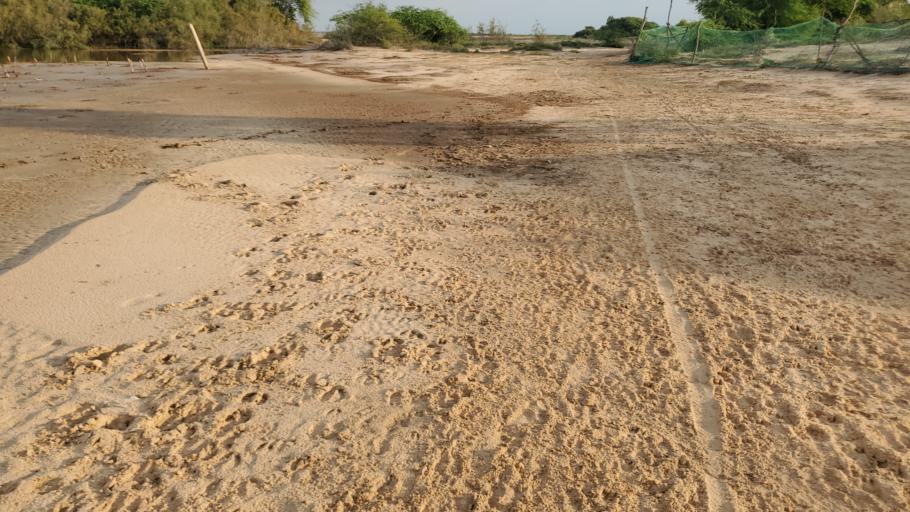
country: SN
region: Saint-Louis
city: Saint-Louis
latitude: 16.0443
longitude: -16.4170
